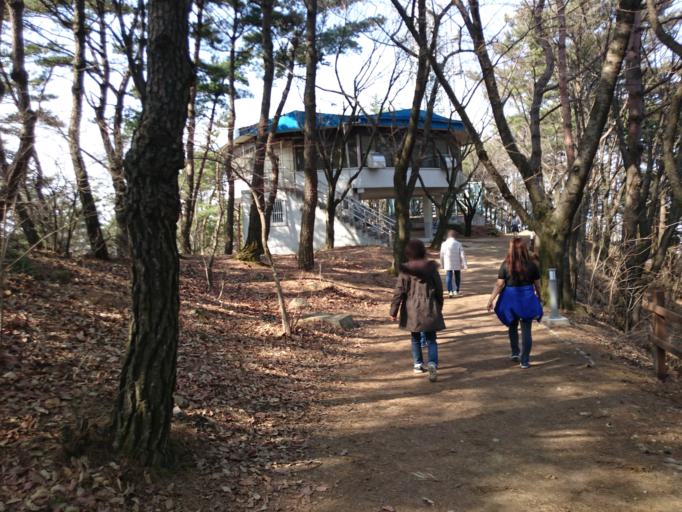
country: KR
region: Daegu
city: Daegu
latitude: 35.8237
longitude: 128.5794
